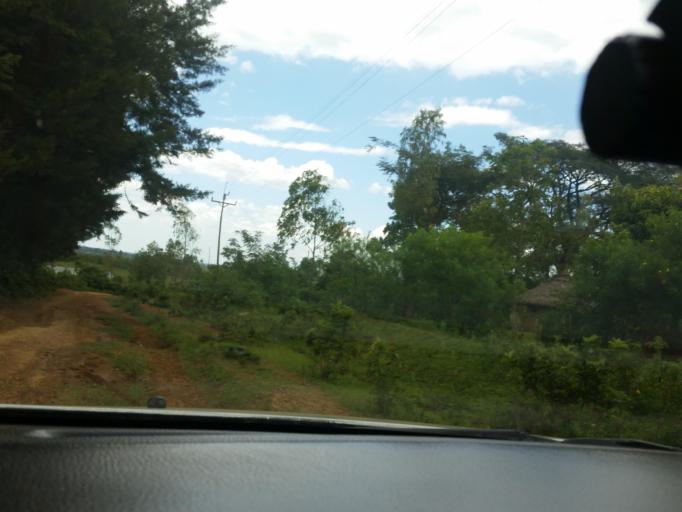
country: KE
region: Siaya
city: Yala
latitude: 0.1089
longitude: 34.4105
